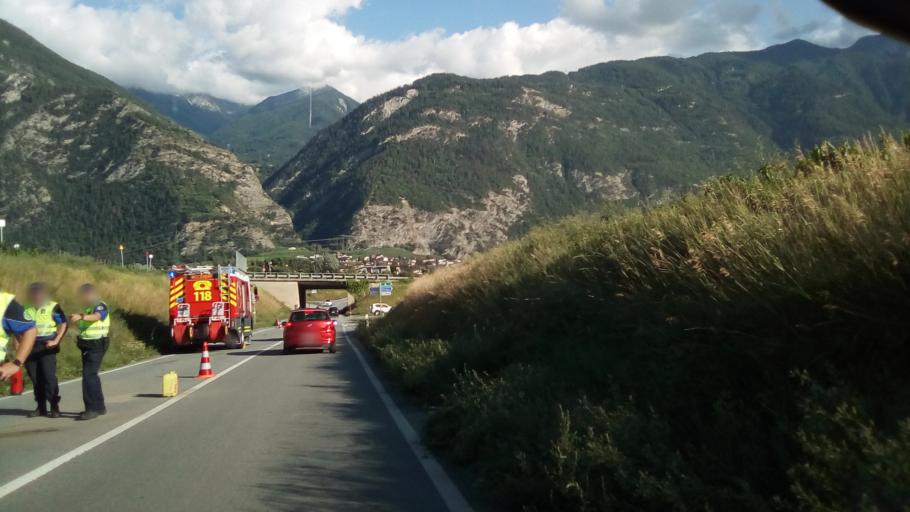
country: CH
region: Valais
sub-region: Martigny District
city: Leytron
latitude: 46.1823
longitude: 7.2156
